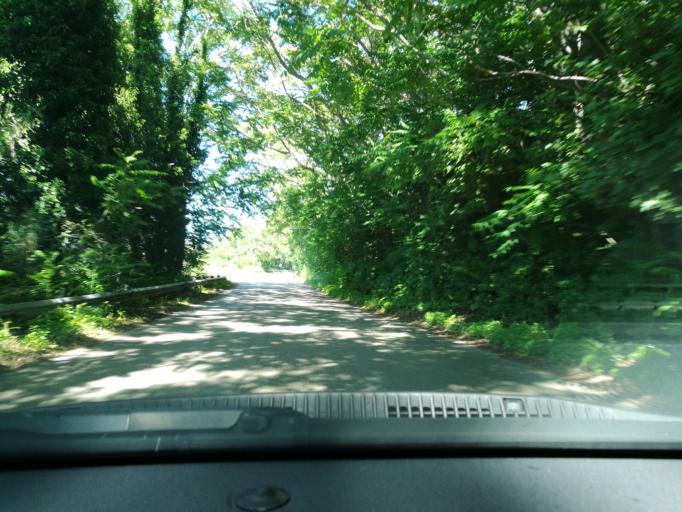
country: IT
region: Abruzzo
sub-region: Provincia di Chieti
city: Vasto
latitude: 42.1647
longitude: 14.6998
